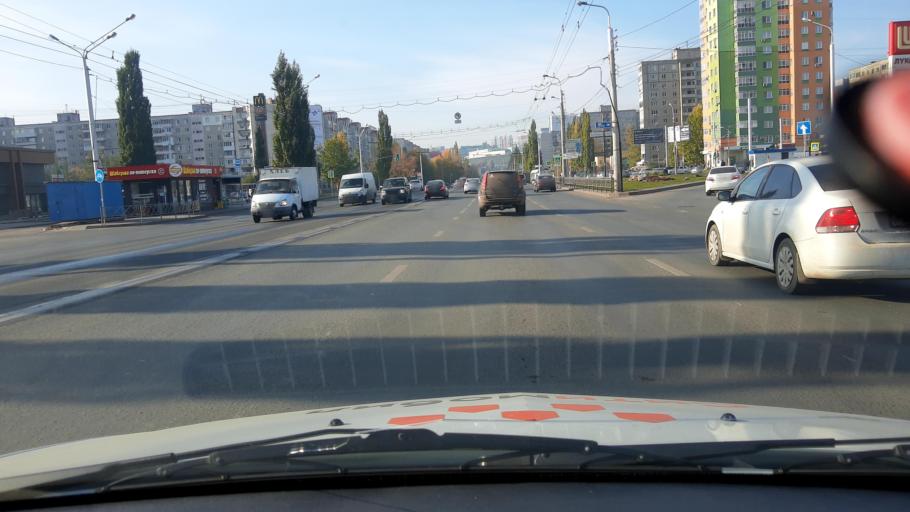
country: RU
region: Bashkortostan
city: Ufa
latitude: 54.7705
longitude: 56.0583
